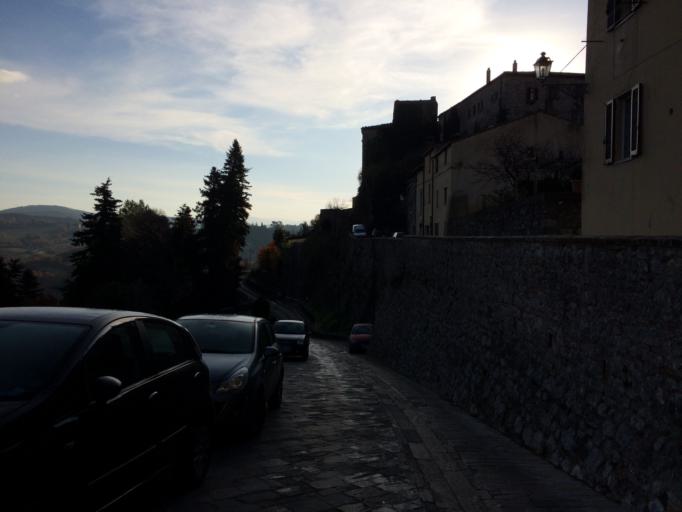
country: IT
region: Umbria
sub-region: Provincia di Terni
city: Amelia
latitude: 42.5595
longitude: 12.4140
